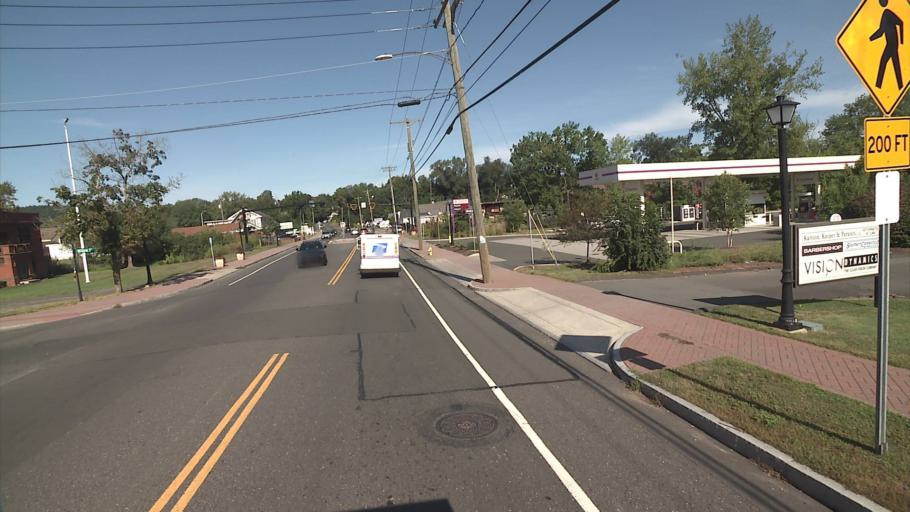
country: US
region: Connecticut
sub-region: New Haven County
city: Cheshire Village
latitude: 41.5075
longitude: -72.9121
